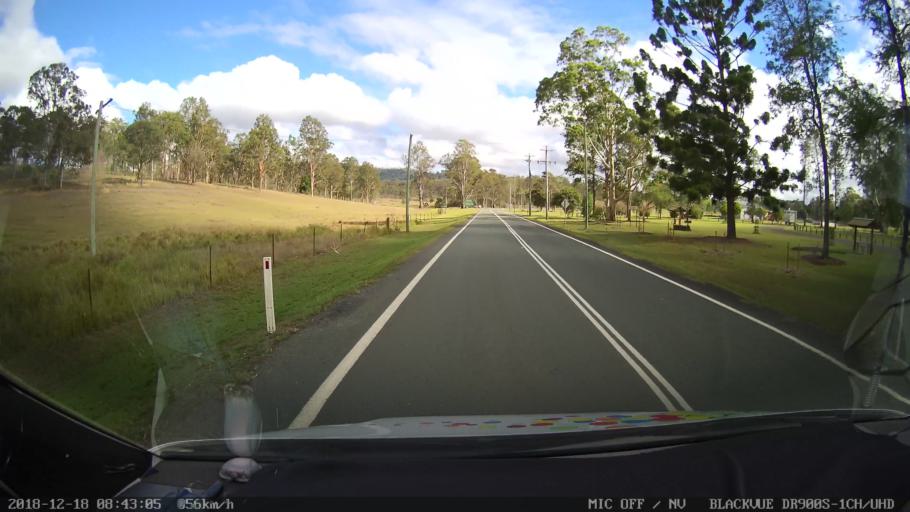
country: AU
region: Queensland
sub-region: Logan
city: Cedar Vale
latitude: -28.2214
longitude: 152.8585
